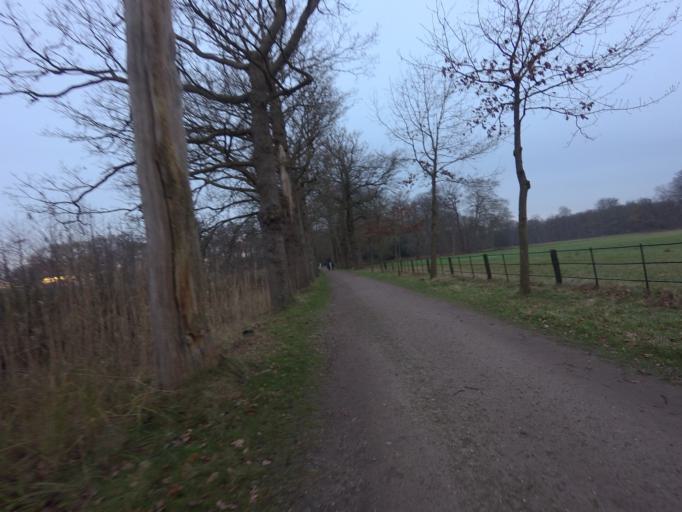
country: NL
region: North Holland
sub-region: Gemeente Bussum
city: Bussum
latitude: 52.2525
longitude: 5.1384
